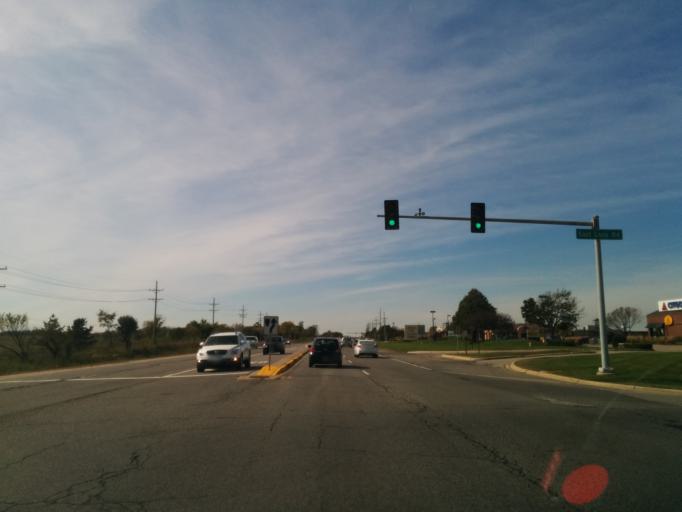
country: US
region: Illinois
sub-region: DuPage County
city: Lisle
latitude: 41.8291
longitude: -88.0964
